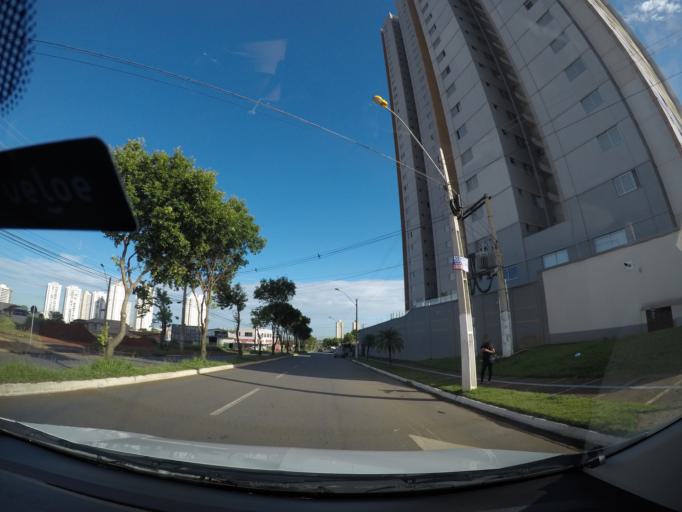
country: BR
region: Goias
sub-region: Goiania
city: Goiania
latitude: -16.7350
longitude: -49.2872
